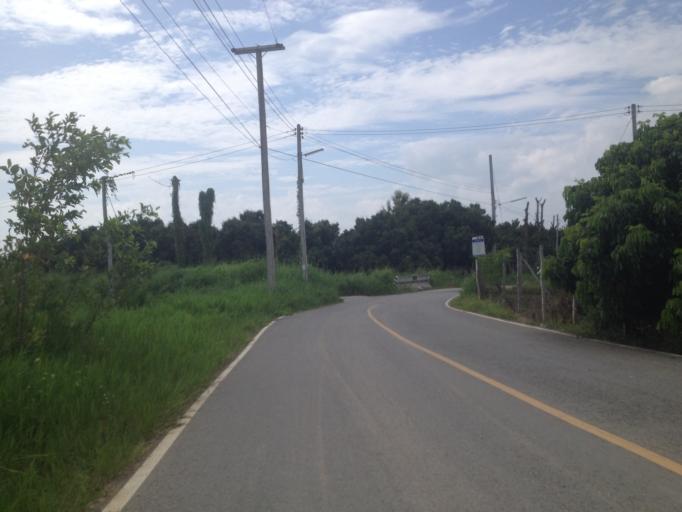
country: TH
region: Chiang Mai
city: Hang Dong
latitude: 18.6682
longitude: 98.9635
